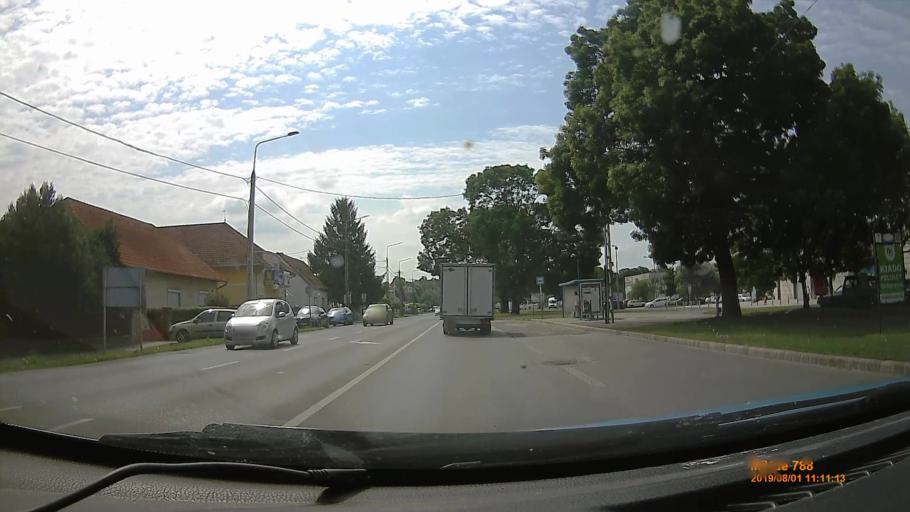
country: HU
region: Baranya
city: Pecs
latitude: 46.0506
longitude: 18.2131
